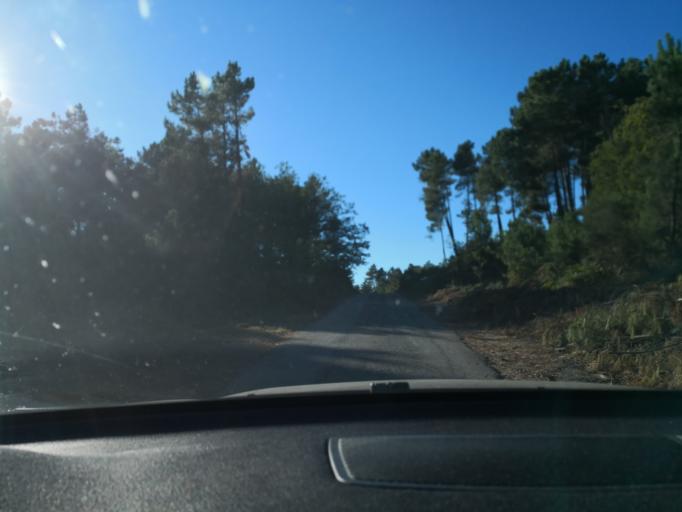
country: PT
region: Vila Real
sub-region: Sabrosa
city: Vilela
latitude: 41.2428
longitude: -7.6190
